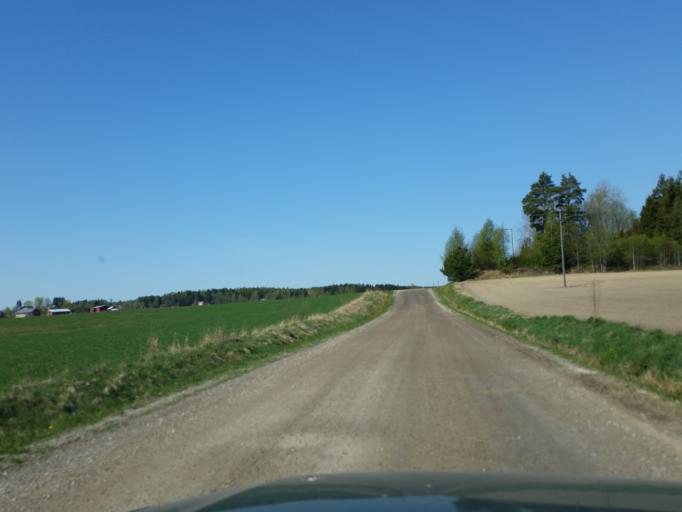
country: FI
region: Uusimaa
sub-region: Raaseporin
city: Karis
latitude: 60.1409
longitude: 23.7177
